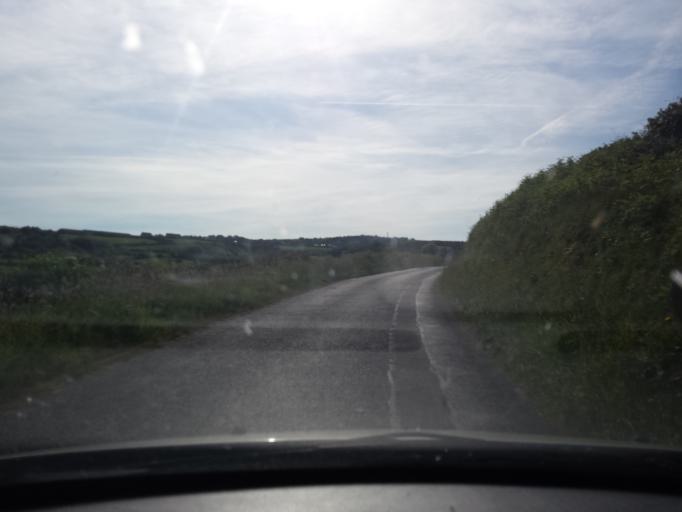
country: FR
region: Lower Normandy
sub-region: Departement de la Manche
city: Beaumont-Hague
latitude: 49.6883
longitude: -1.9299
